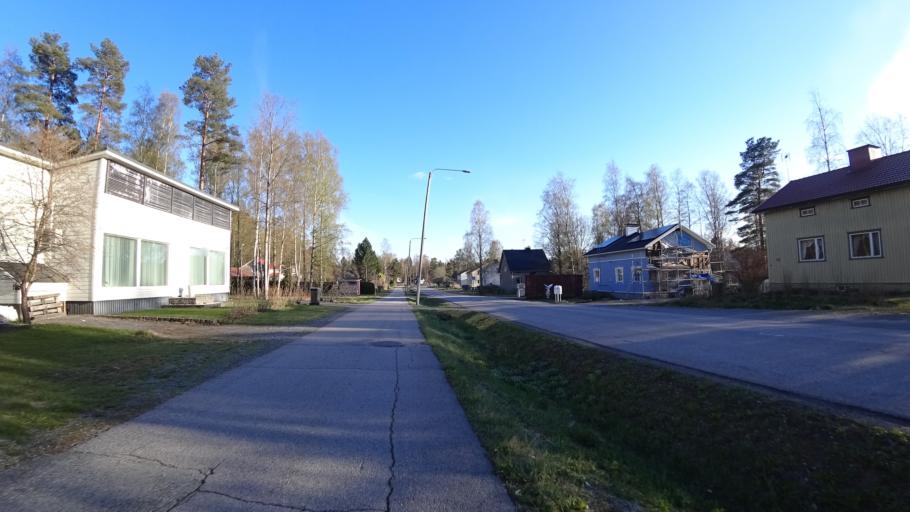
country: FI
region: Pirkanmaa
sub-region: Tampere
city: Yloejaervi
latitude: 61.5081
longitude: 23.5938
